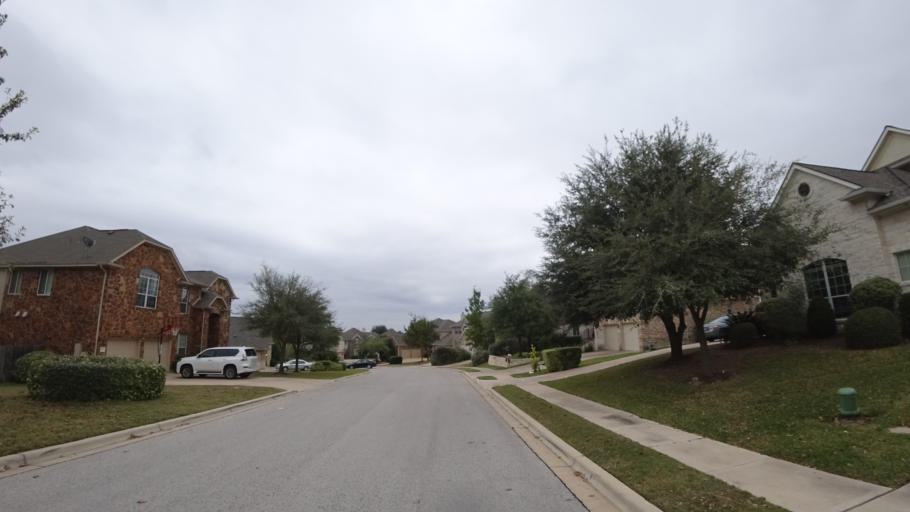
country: US
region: Texas
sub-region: Travis County
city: Bee Cave
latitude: 30.3535
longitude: -97.9040
